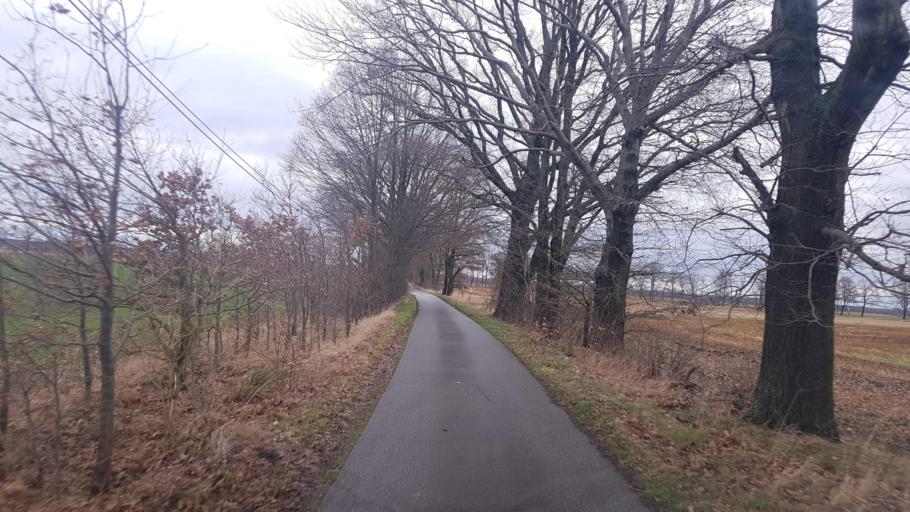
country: DE
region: Brandenburg
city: Plessa
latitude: 51.4499
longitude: 13.6511
